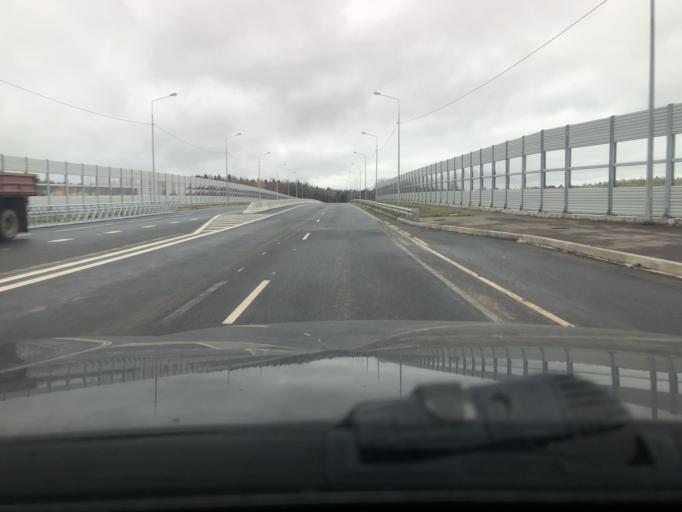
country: RU
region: Moskovskaya
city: Semkhoz
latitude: 56.3249
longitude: 38.0769
